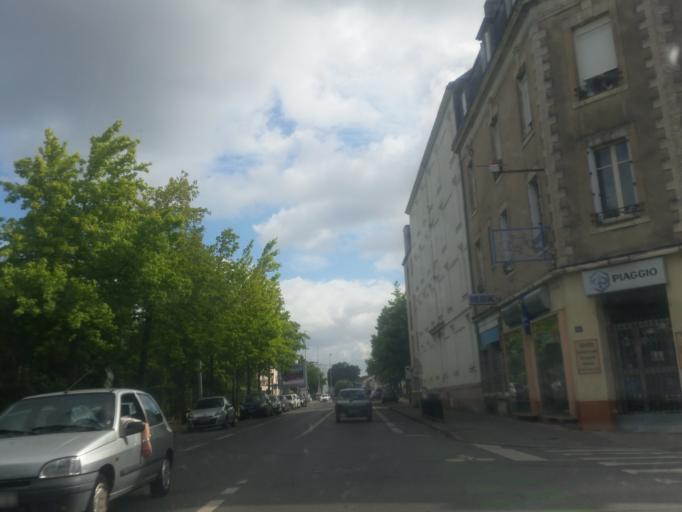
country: FR
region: Pays de la Loire
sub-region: Departement de la Loire-Atlantique
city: Saint-Sebastien-sur-Loire
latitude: 47.2294
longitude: -1.5249
